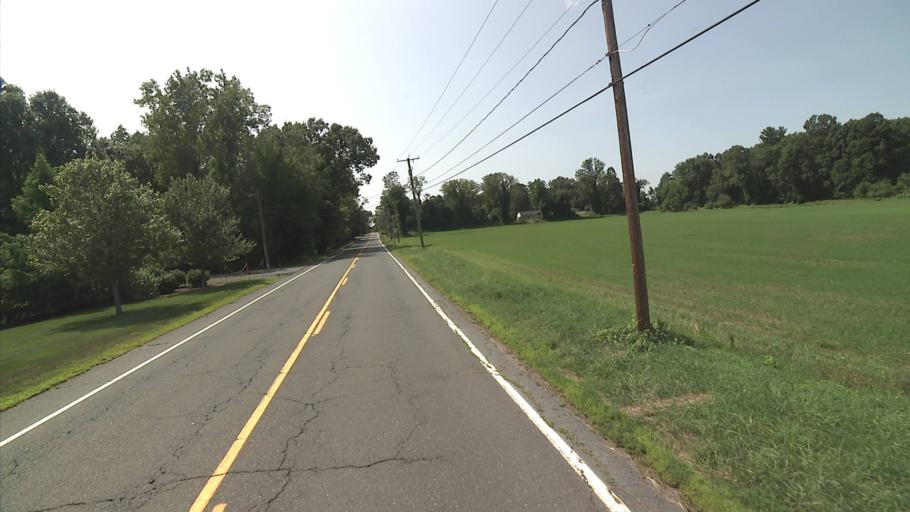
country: US
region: Connecticut
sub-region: Hartford County
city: Windsor Locks
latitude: 41.8948
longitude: -72.5989
